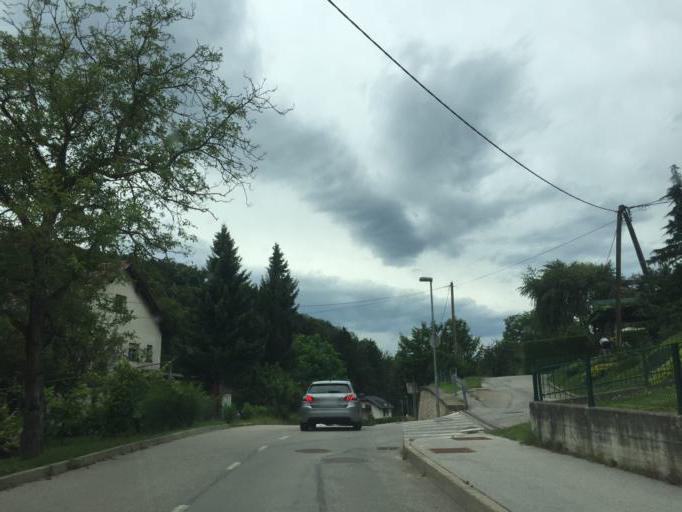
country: SI
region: Gornja Radgona
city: Gornja Radgona
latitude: 46.6740
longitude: 15.9884
